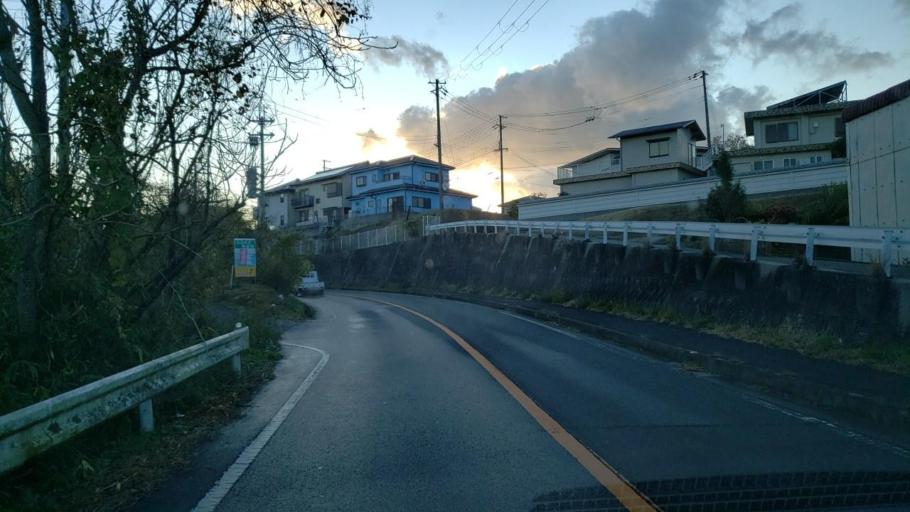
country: JP
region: Hyogo
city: Sumoto
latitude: 34.3947
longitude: 134.8115
